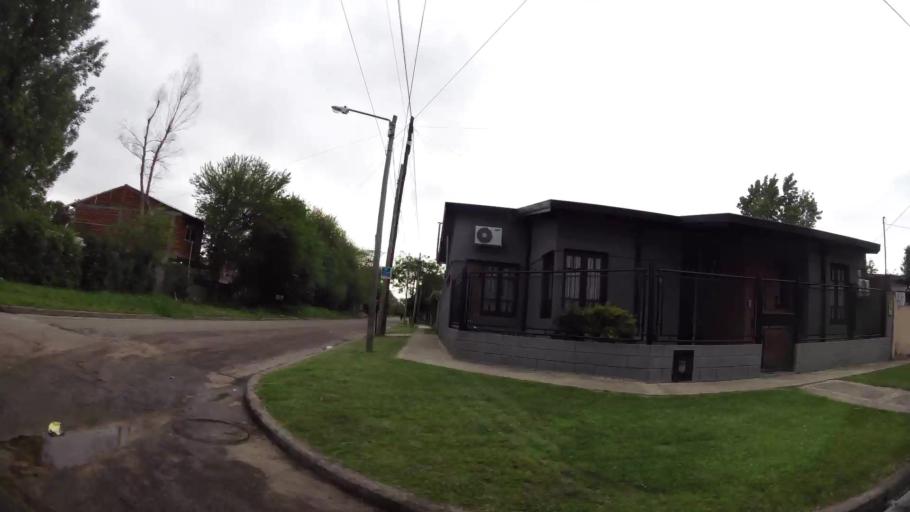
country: AR
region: Buenos Aires
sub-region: Partido de Quilmes
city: Quilmes
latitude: -34.7993
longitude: -58.2717
